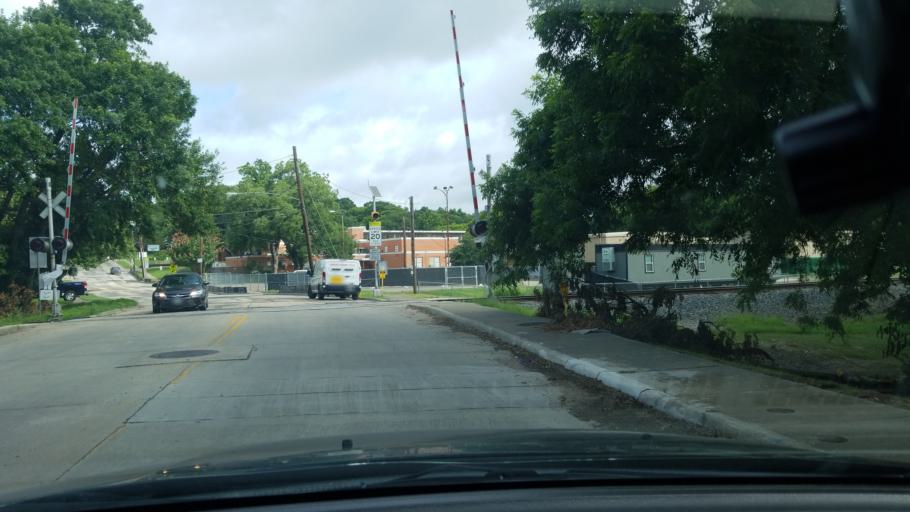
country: US
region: Texas
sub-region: Dallas County
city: Highland Park
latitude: 32.8120
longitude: -96.7093
